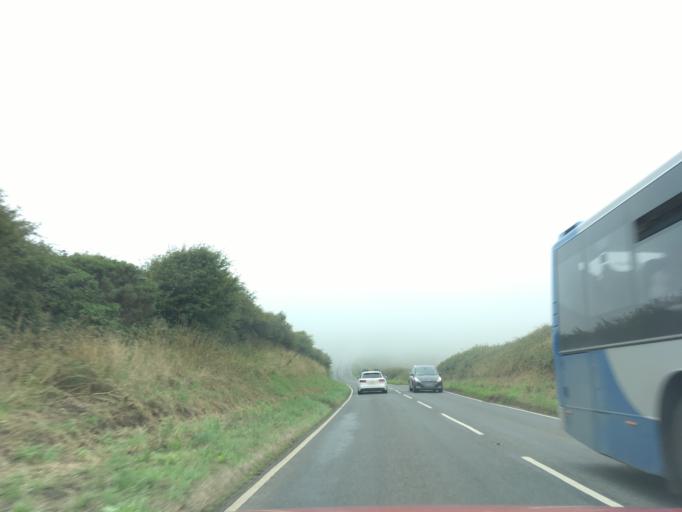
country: GB
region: Wales
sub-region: Pembrokeshire
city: Llanrhian
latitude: 51.8722
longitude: -5.1548
